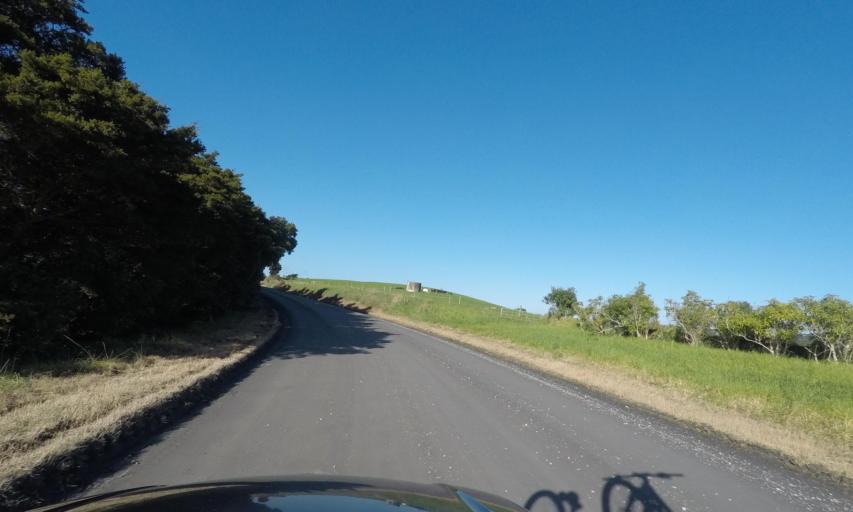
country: NZ
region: Auckland
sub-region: Auckland
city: Wellsford
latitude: -36.1538
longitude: 174.6014
